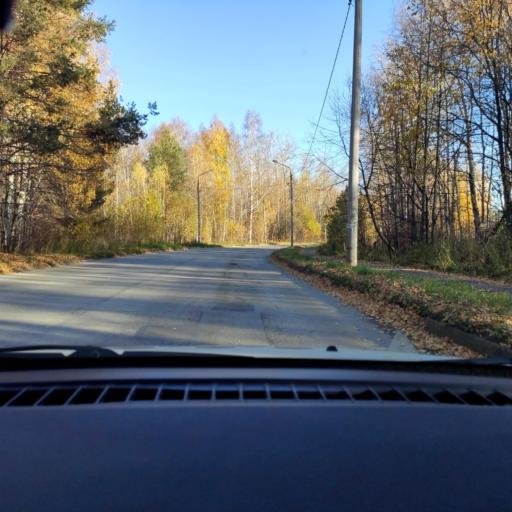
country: RU
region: Perm
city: Perm
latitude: 58.0812
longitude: 56.3641
